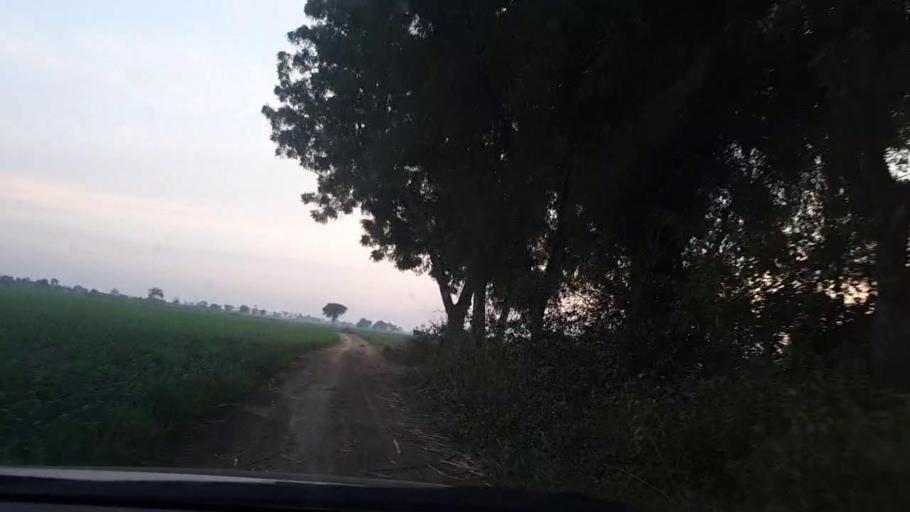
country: PK
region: Sindh
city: Sakrand
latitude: 26.1973
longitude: 68.3247
